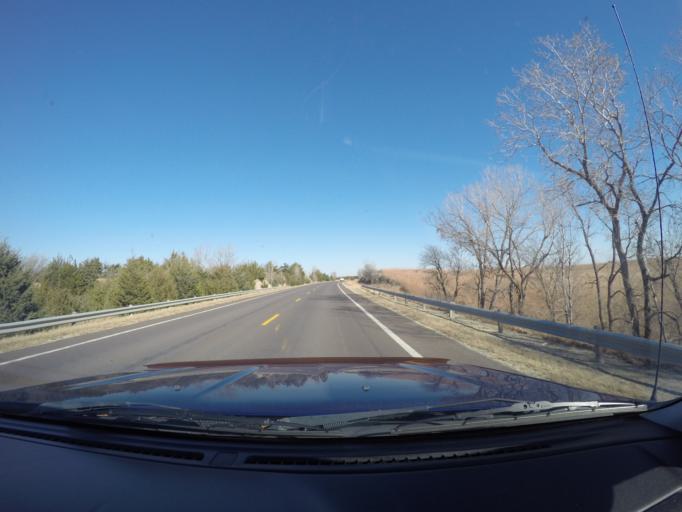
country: US
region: Kansas
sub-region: Marshall County
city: Blue Rapids
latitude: 39.4511
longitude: -96.7641
